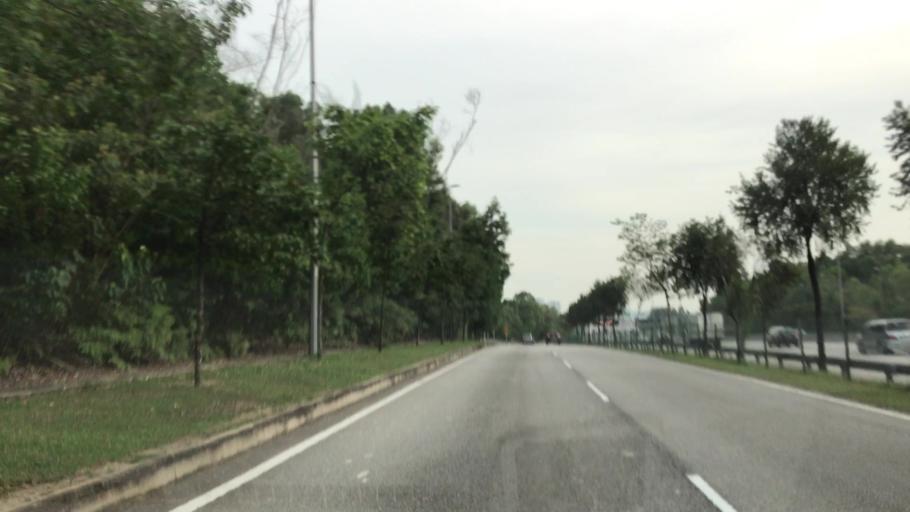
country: MY
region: Kuala Lumpur
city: Kuala Lumpur
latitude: 3.0795
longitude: 101.6919
